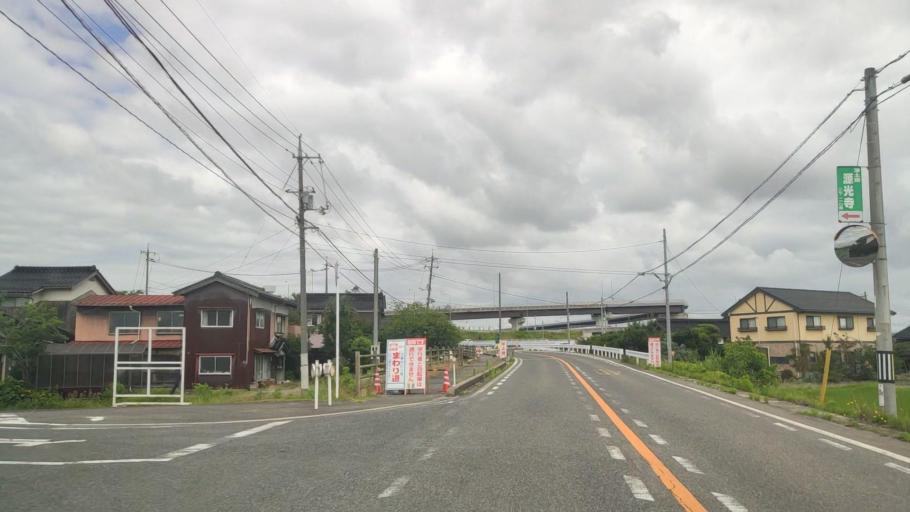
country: JP
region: Tottori
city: Yonago
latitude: 35.4234
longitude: 133.4023
